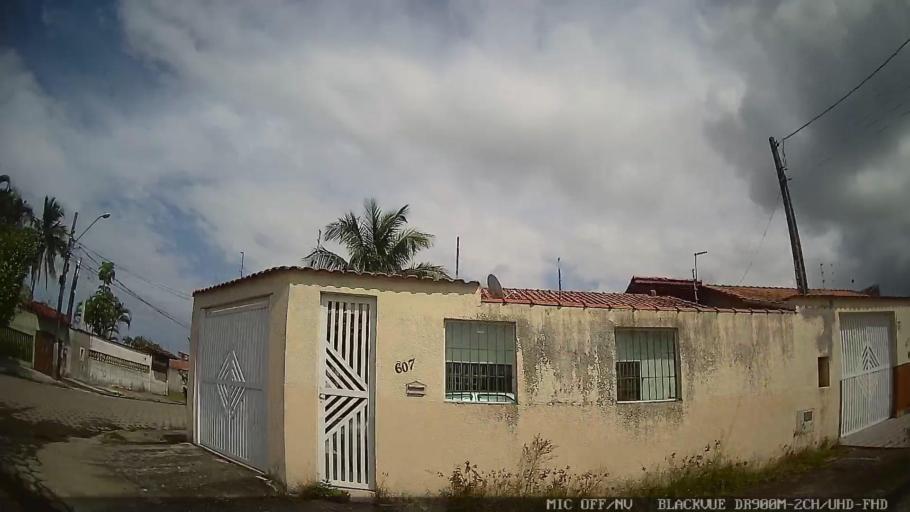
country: BR
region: Sao Paulo
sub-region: Itanhaem
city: Itanhaem
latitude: -24.2005
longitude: -46.8379
